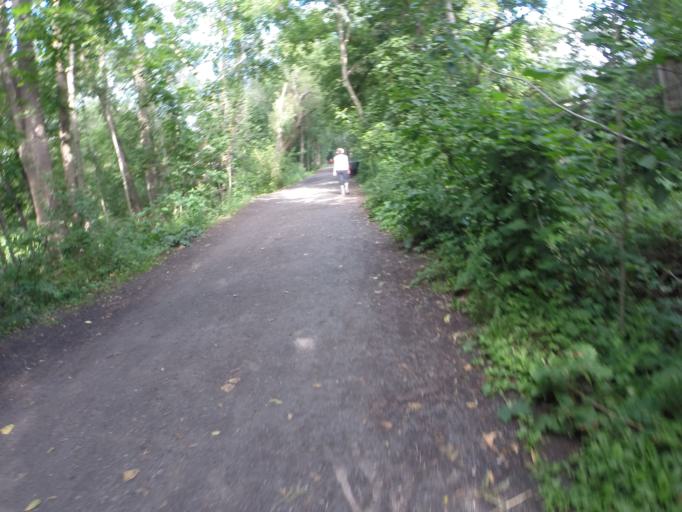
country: CA
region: Ontario
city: Toronto
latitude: 43.6983
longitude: -79.4064
